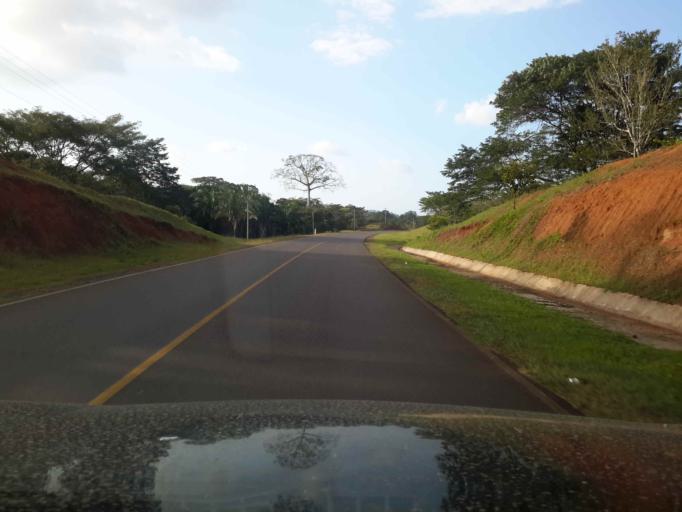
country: NI
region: Rio San Juan
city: San Carlos
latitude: 11.1722
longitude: -84.6747
